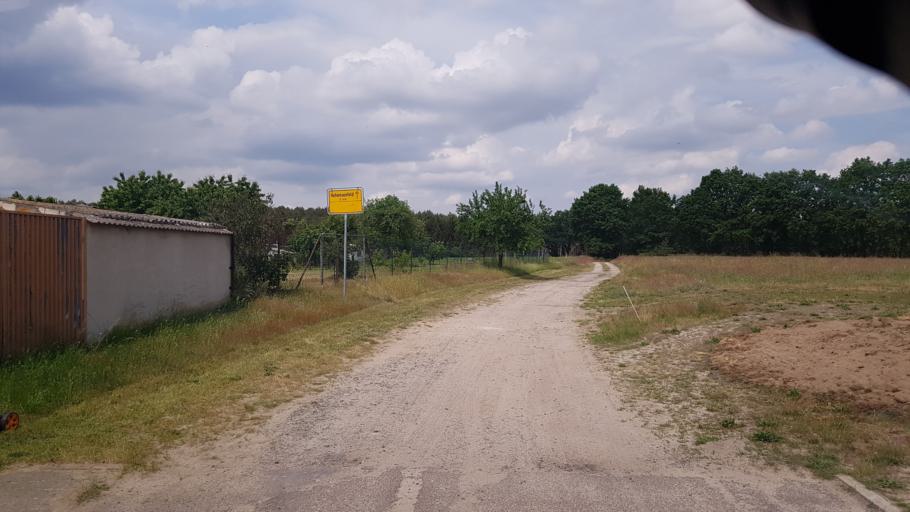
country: DE
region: Brandenburg
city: Ihlow
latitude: 51.8645
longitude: 13.2932
